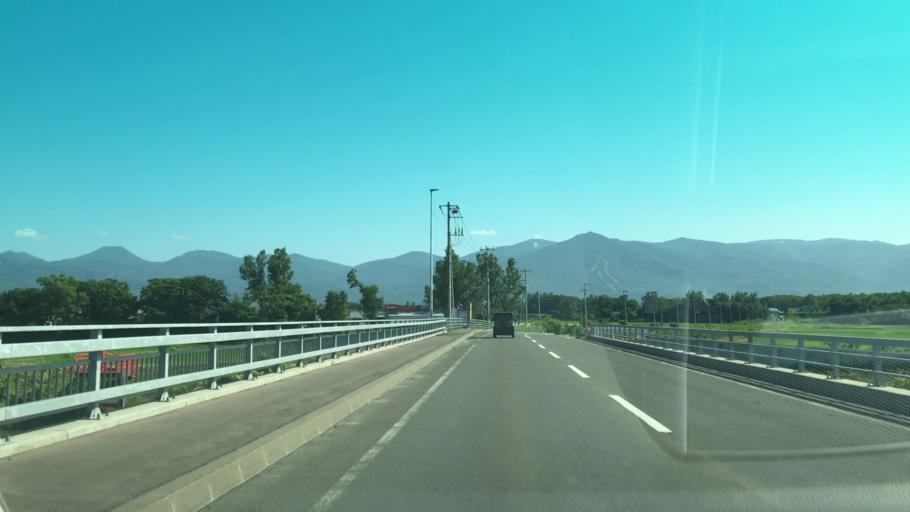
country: JP
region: Hokkaido
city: Iwanai
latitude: 43.0218
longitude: 140.5480
